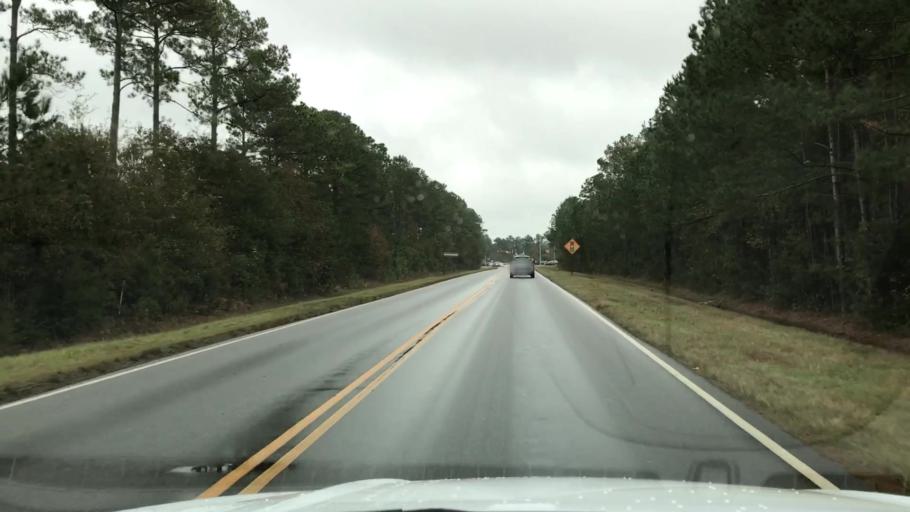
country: US
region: South Carolina
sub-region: Horry County
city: Myrtle Beach
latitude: 33.7546
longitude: -78.8712
